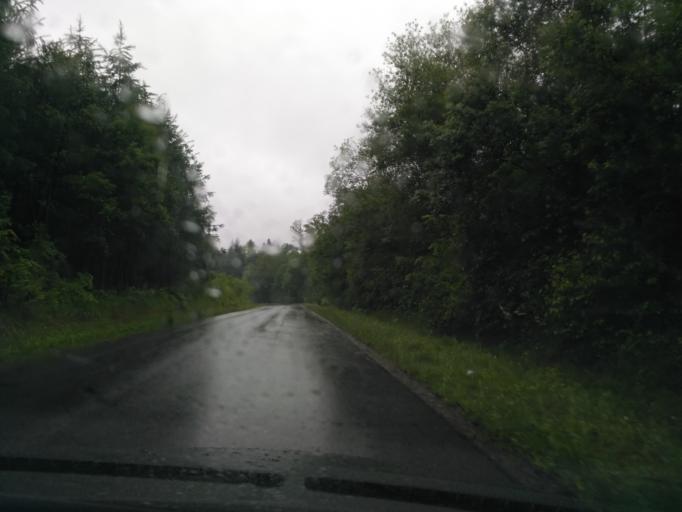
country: PL
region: Subcarpathian Voivodeship
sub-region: Powiat jasielski
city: Debowiec
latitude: 49.6643
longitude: 21.4419
